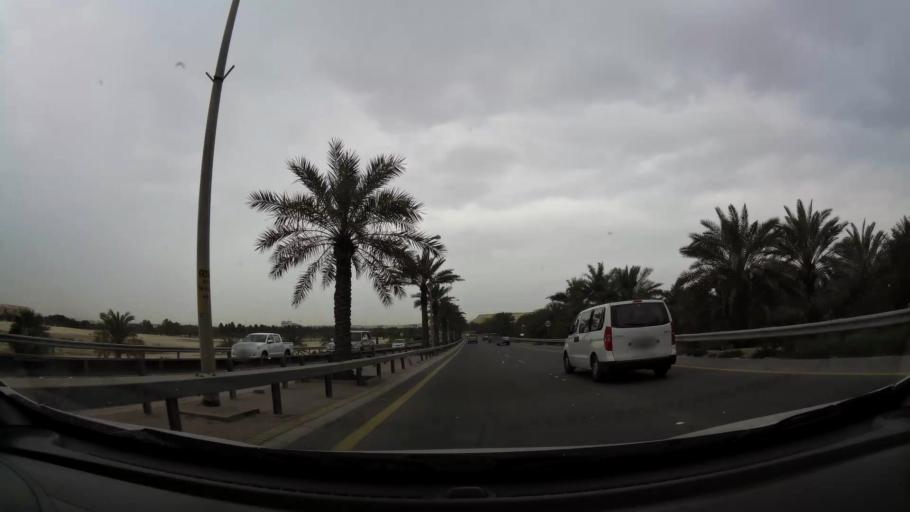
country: BH
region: Northern
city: Ar Rifa'
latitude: 26.1154
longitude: 50.5372
